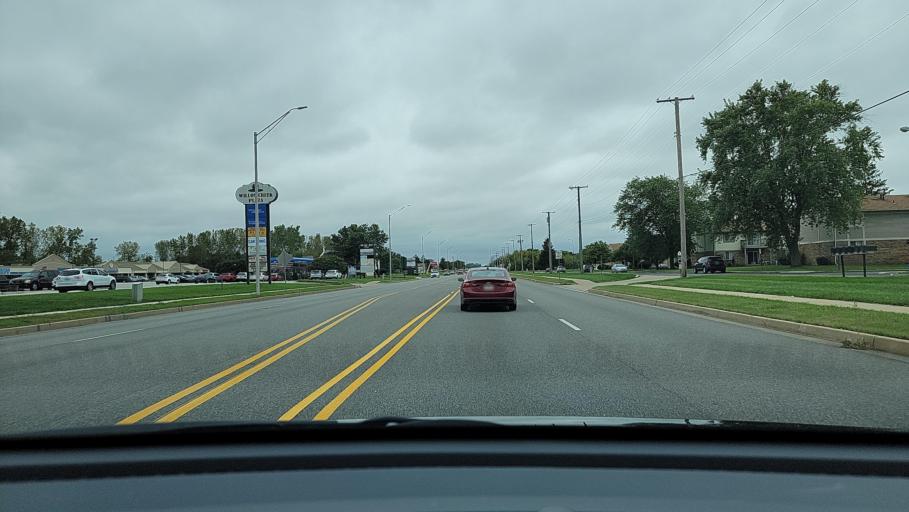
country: US
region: Indiana
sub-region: Porter County
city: Portage
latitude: 41.5573
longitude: -87.1828
